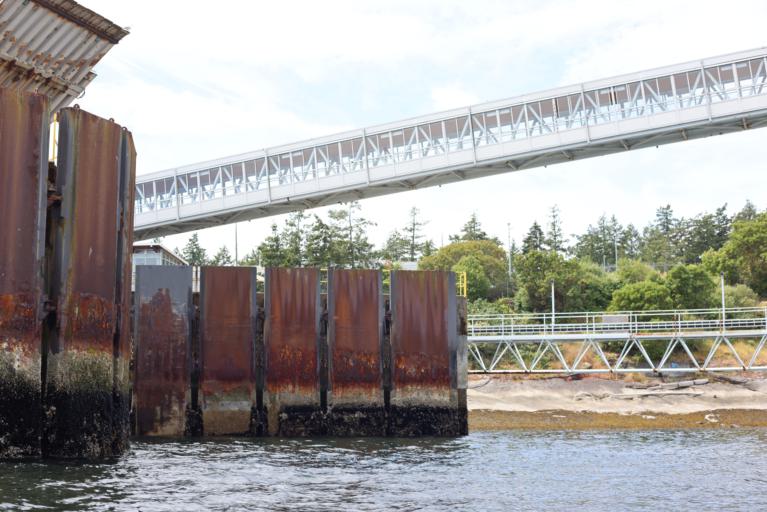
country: CA
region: British Columbia
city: Nanaimo
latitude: 49.1637
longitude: -123.8911
